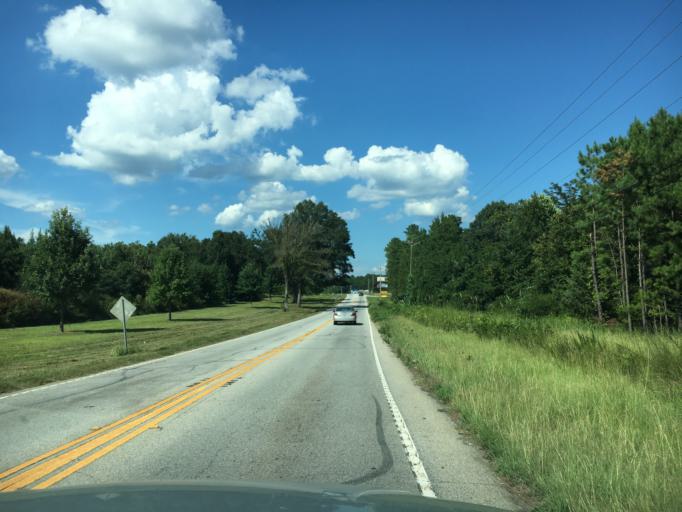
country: US
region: South Carolina
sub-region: Laurens County
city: Clinton
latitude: 34.4945
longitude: -81.8661
